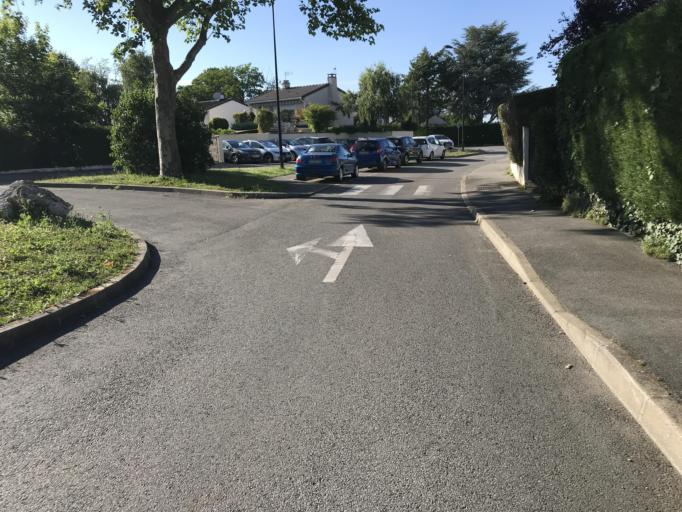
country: FR
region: Ile-de-France
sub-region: Departement de l'Essonne
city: Nozay
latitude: 48.6631
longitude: 2.2352
